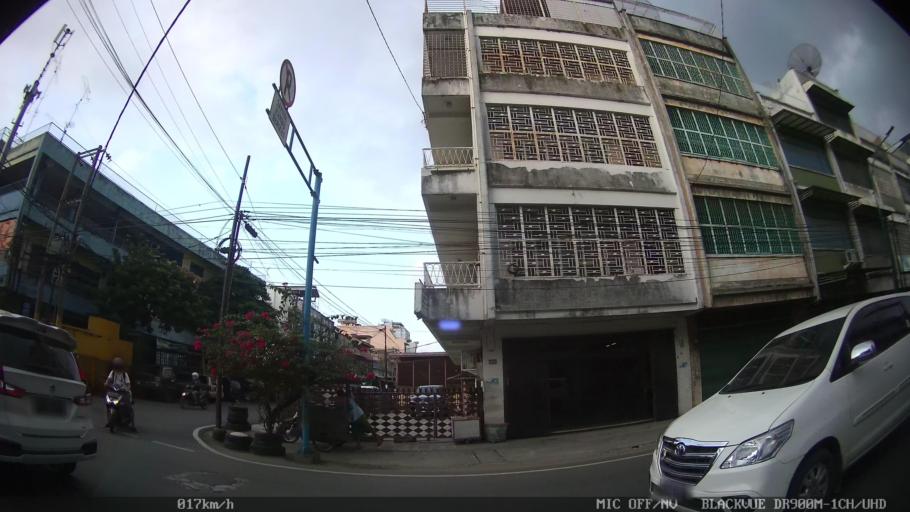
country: ID
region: North Sumatra
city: Medan
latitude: 3.5813
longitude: 98.6884
